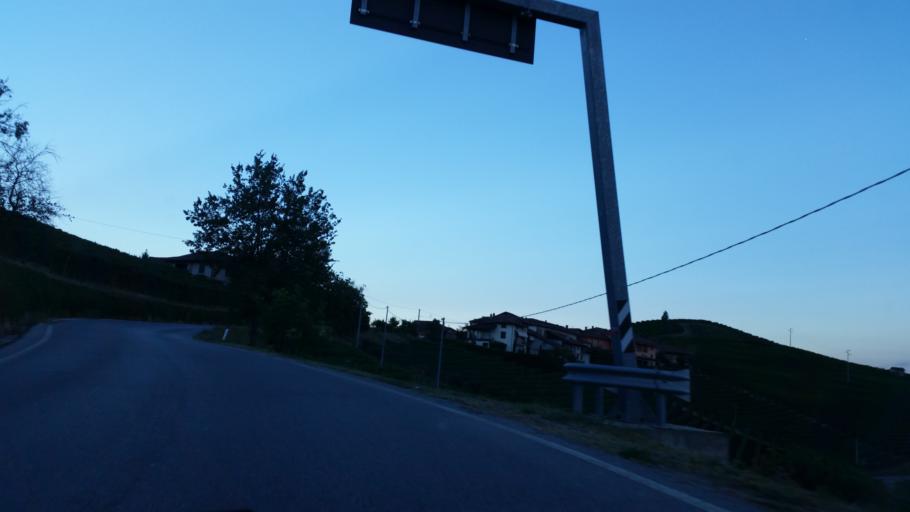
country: IT
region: Piedmont
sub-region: Provincia di Cuneo
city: Barbaresco
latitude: 44.7205
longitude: 8.0838
